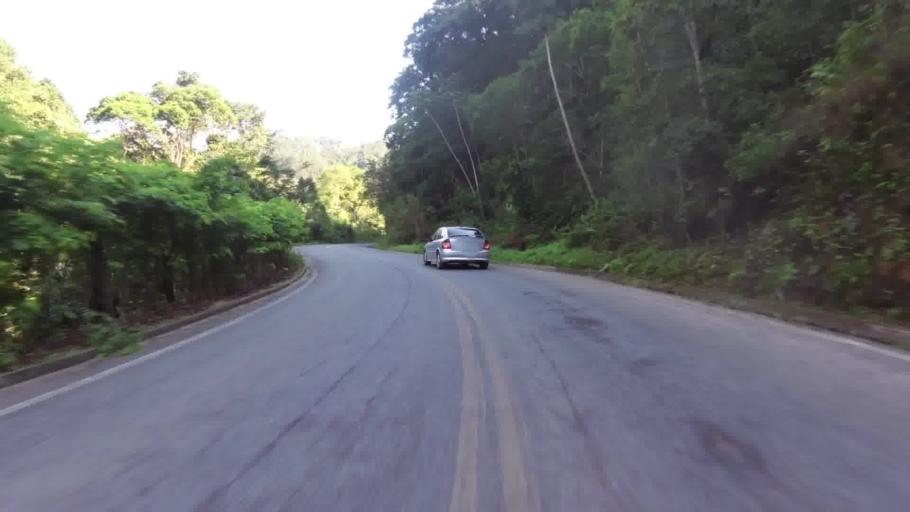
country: BR
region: Espirito Santo
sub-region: Alfredo Chaves
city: Alfredo Chaves
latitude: -20.5787
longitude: -40.7956
